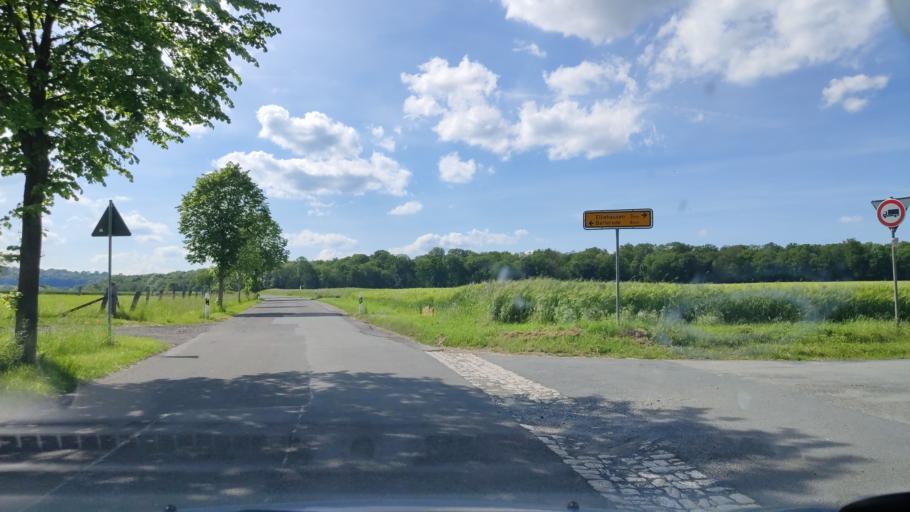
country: DE
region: Lower Saxony
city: Dransfeld
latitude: 51.5404
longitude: 9.8193
